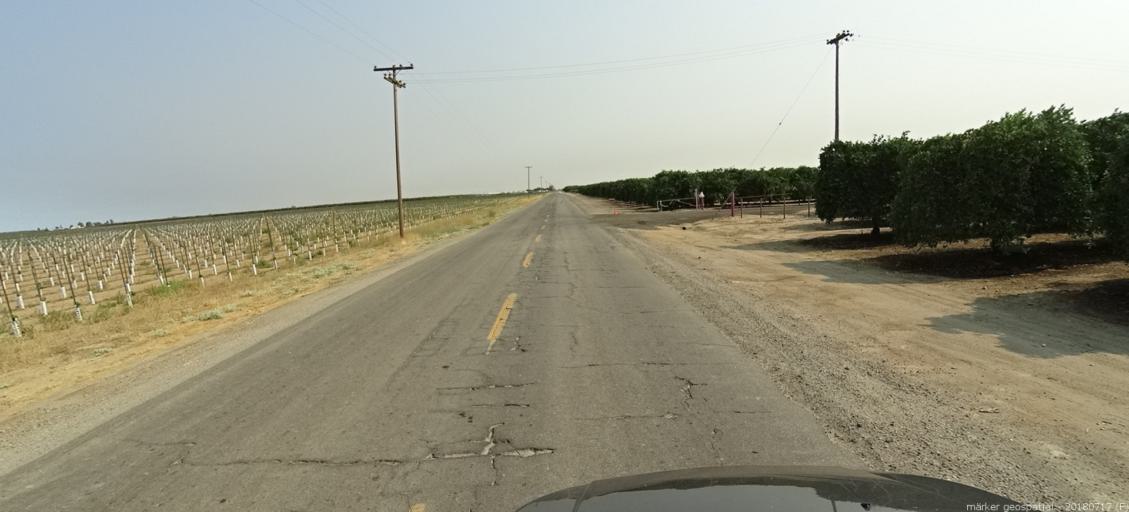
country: US
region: California
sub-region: Madera County
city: Madera Acres
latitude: 37.0758
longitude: -120.1108
